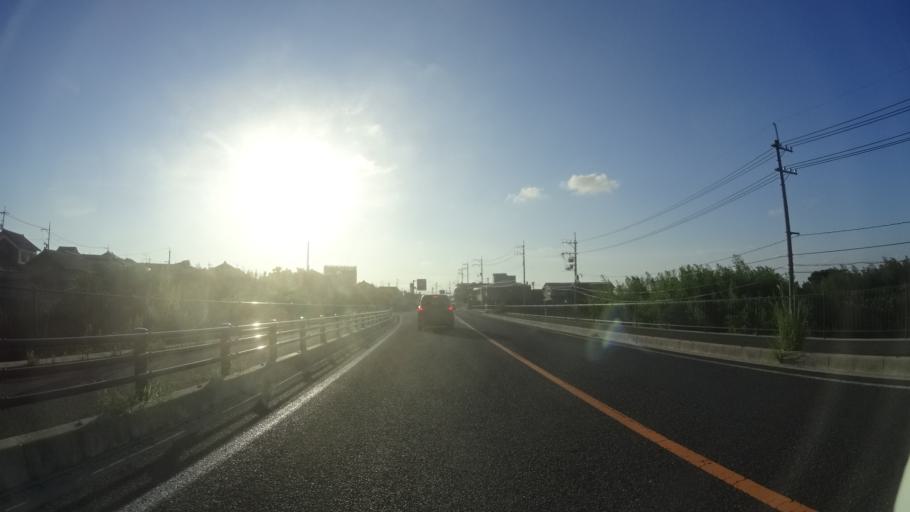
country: JP
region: Tottori
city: Yonago
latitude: 35.5131
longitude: 133.5047
